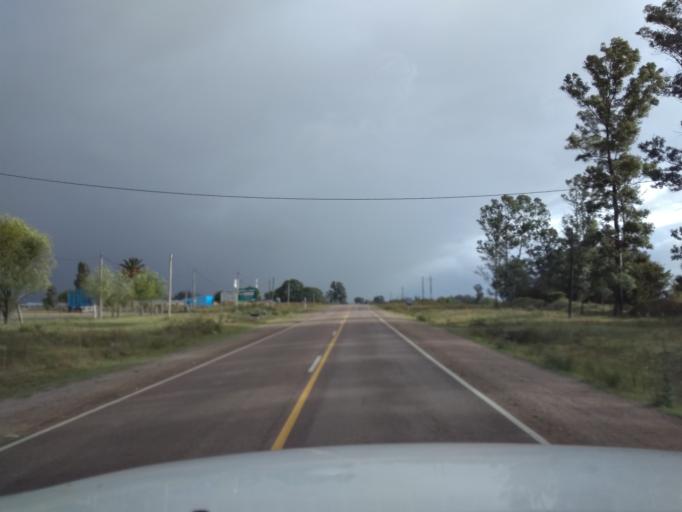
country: UY
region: Canelones
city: Tala
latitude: -34.3713
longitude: -55.7850
